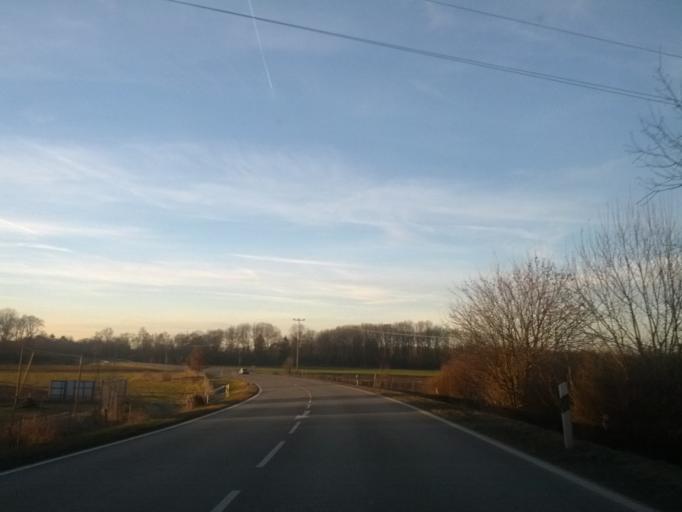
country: DE
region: Bavaria
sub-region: Swabia
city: Heimertingen
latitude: 48.0329
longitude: 10.1439
